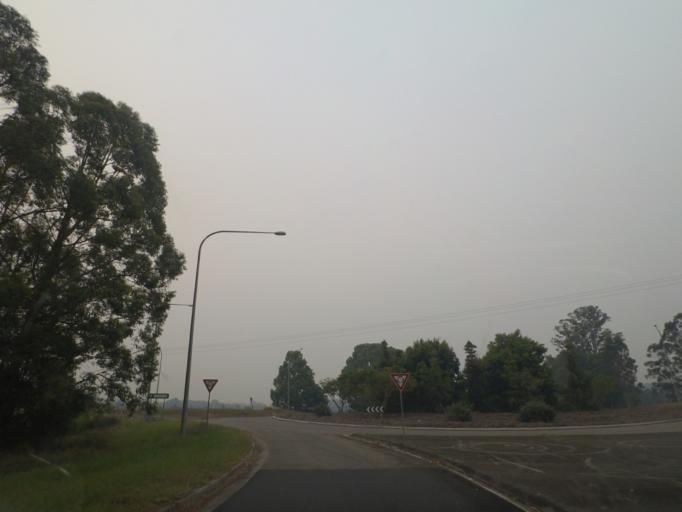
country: AU
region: New South Wales
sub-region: Coffs Harbour
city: Bonville
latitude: -30.3912
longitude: 153.0305
